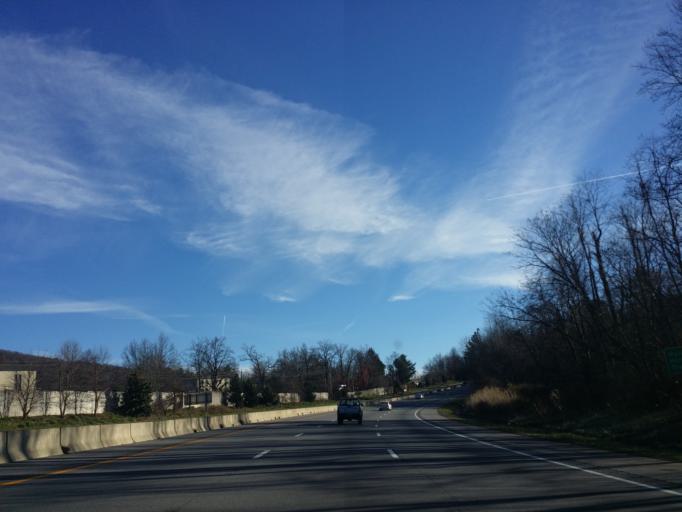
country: US
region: North Carolina
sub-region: Buncombe County
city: Black Mountain
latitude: 35.6208
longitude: -82.2768
